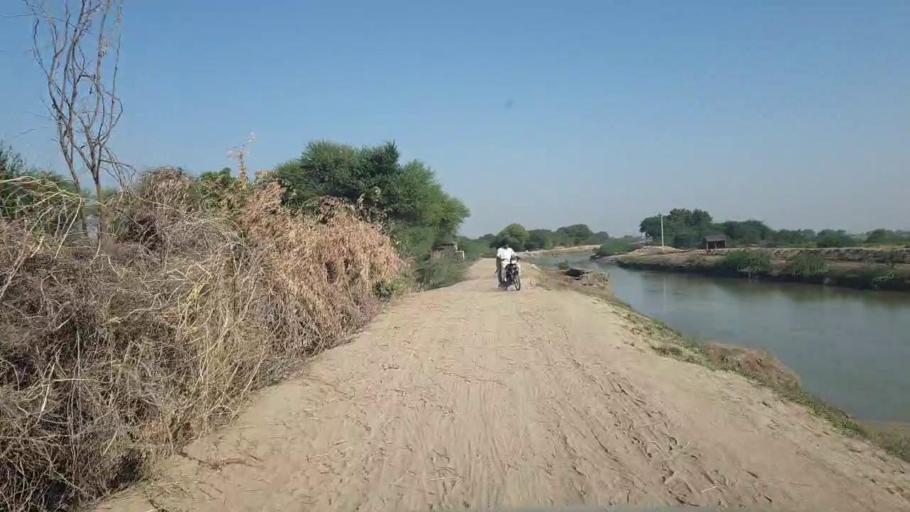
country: PK
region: Sindh
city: Badin
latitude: 24.7222
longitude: 68.8029
